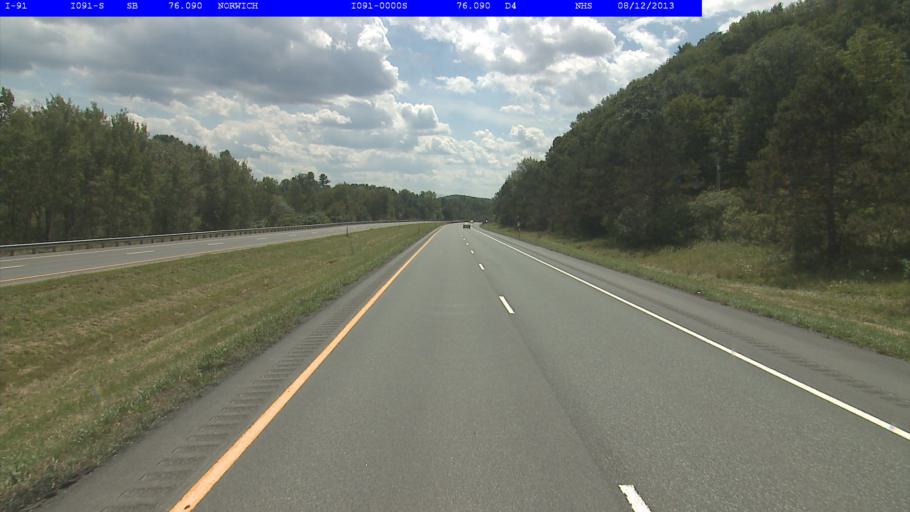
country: US
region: New Hampshire
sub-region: Grafton County
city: Hanover
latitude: 43.7201
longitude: -72.2914
